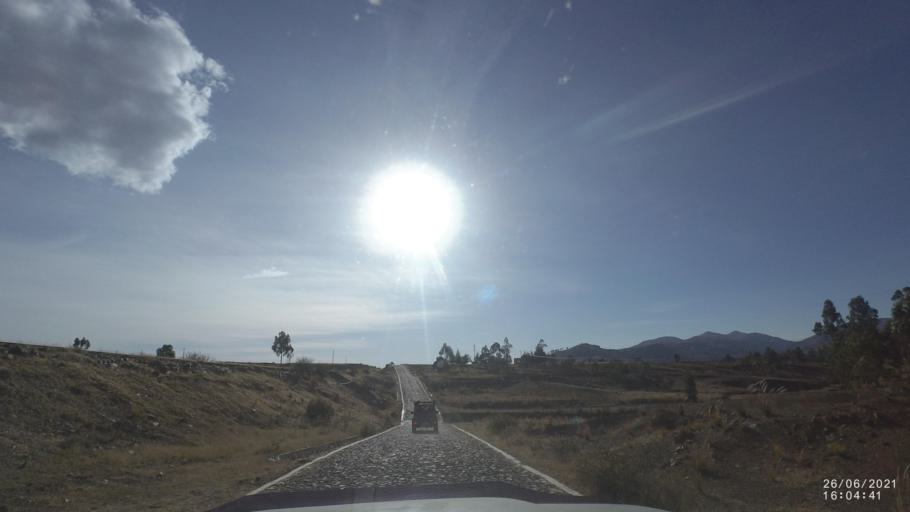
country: BO
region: Cochabamba
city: Arani
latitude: -17.8309
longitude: -65.7584
